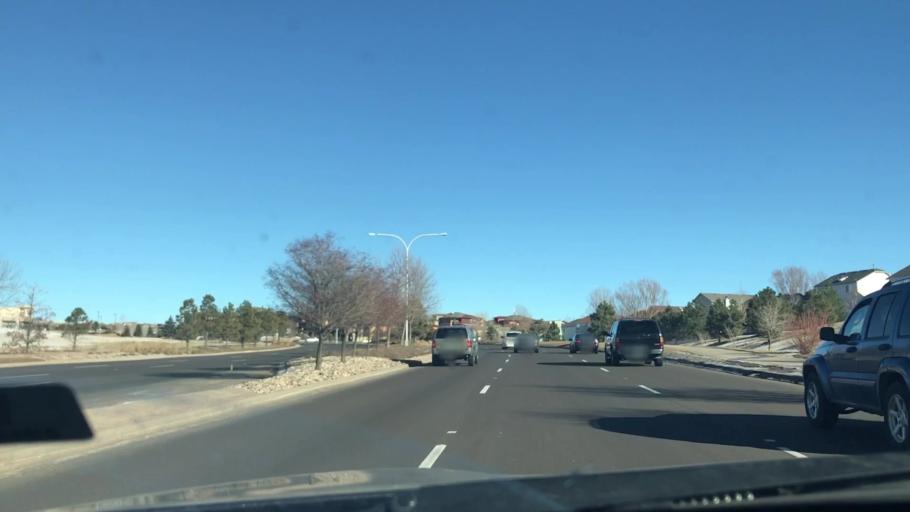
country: US
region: Colorado
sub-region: El Paso County
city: Black Forest
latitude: 38.9658
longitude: -104.7491
